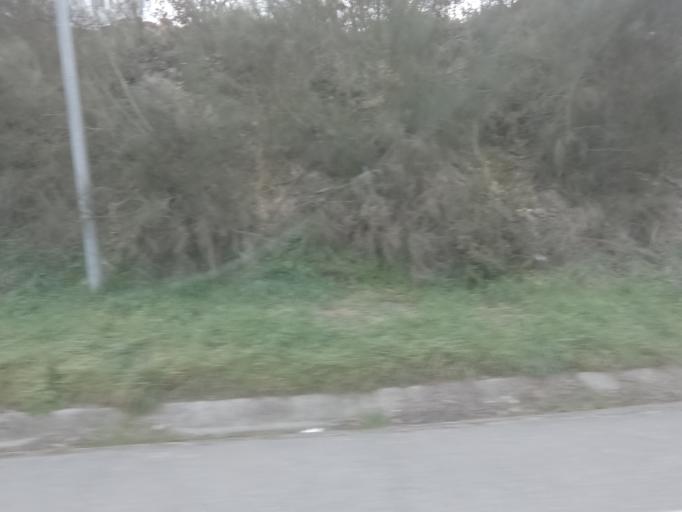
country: ES
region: Galicia
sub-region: Provincia de Ourense
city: Allariz
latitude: 42.1955
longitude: -7.7986
